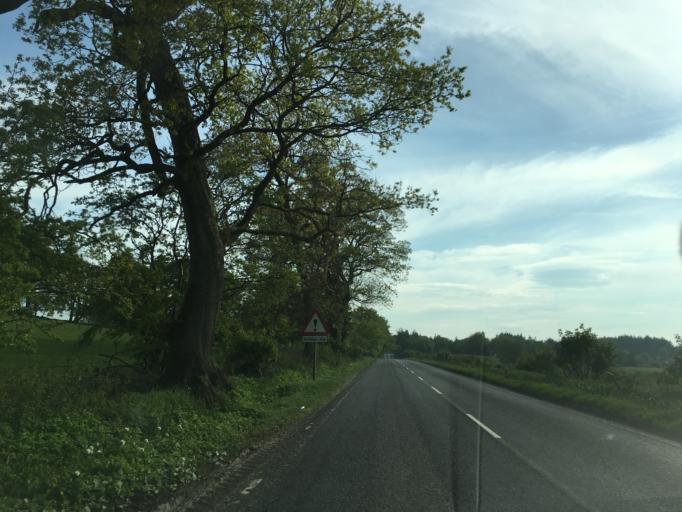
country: GB
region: Scotland
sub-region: Midlothian
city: Penicuik
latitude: 55.7718
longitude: -3.2450
